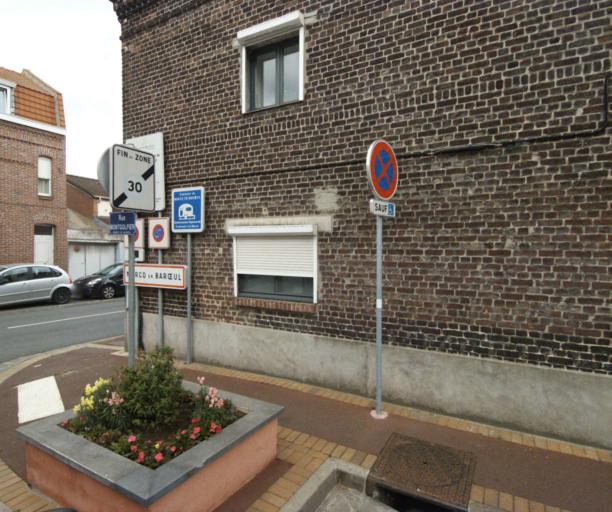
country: FR
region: Nord-Pas-de-Calais
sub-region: Departement du Nord
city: Marquette-lez-Lille
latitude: 50.6668
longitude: 3.0700
